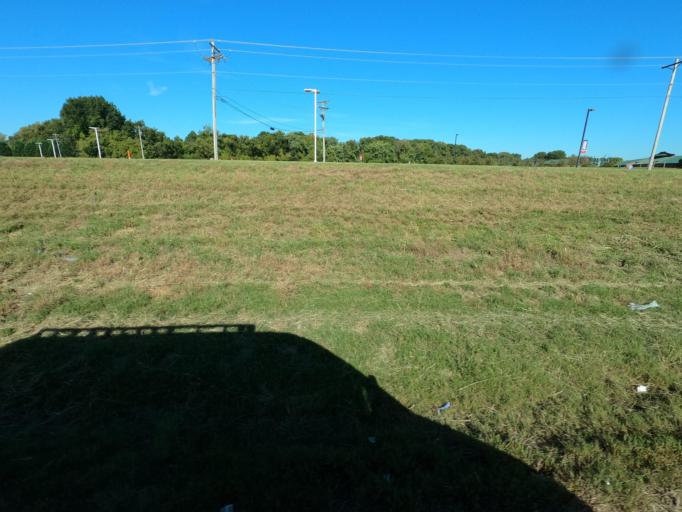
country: US
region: Tennessee
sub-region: Tipton County
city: Covington
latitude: 35.5282
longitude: -89.6858
